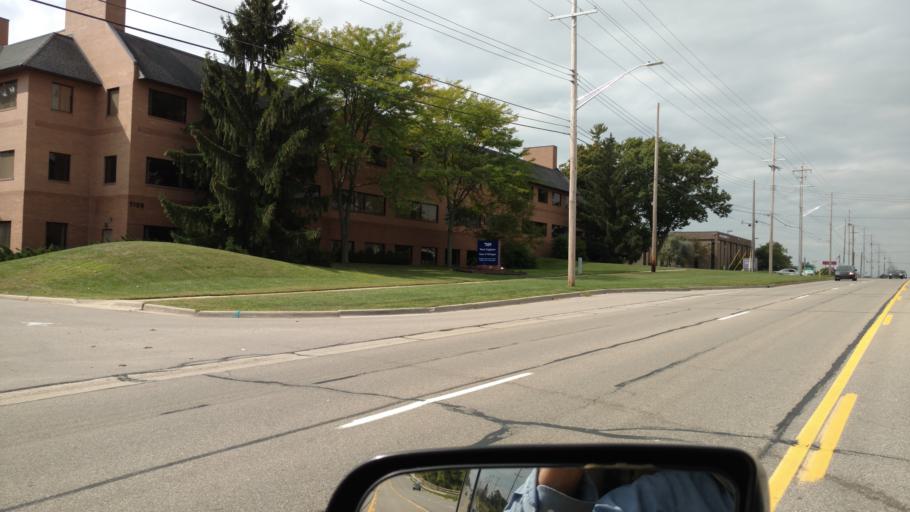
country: US
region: Michigan
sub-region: Eaton County
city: Waverly
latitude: 42.7411
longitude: -84.6529
